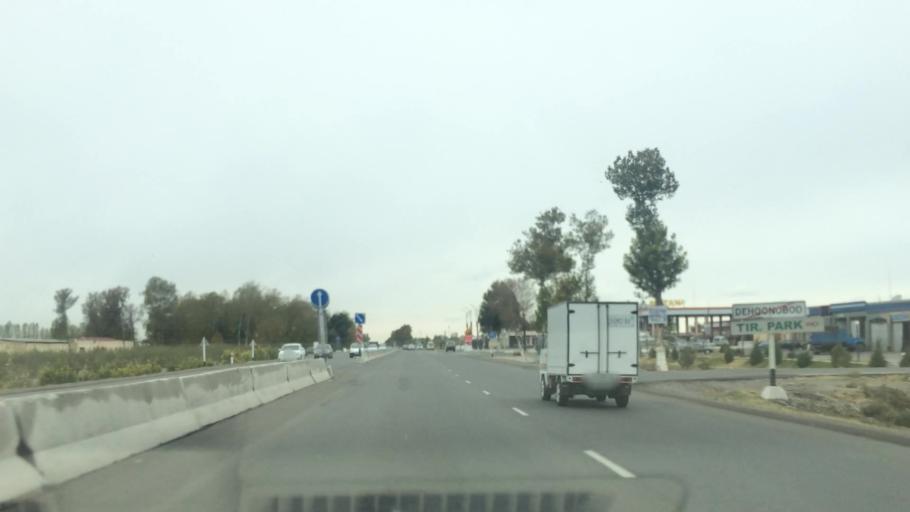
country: UZ
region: Samarqand
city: Jomboy
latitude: 39.7207
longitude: 67.1201
